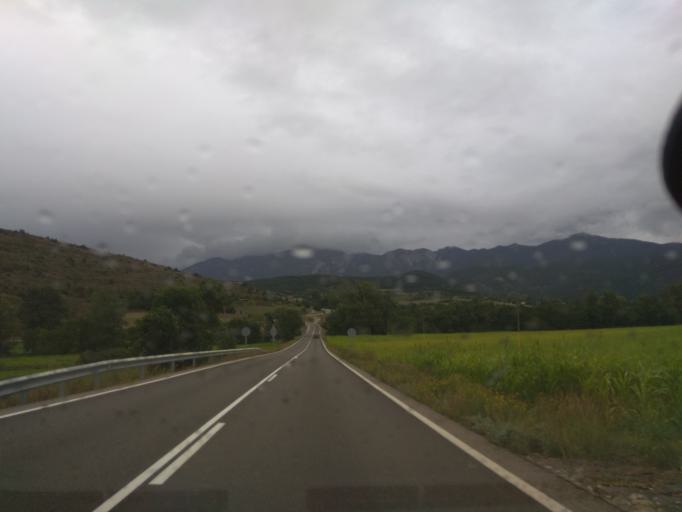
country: ES
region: Catalonia
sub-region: Provincia de Lleida
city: Bellver de Cerdanya
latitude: 42.3666
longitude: 1.7974
